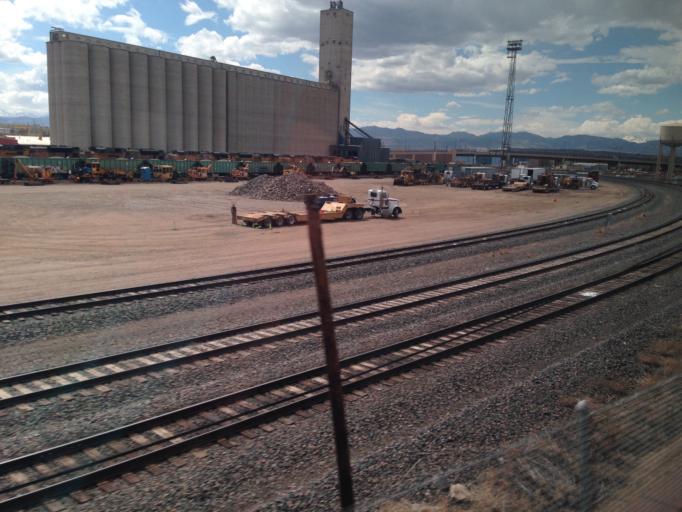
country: US
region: Colorado
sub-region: Adams County
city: Twin Lakes
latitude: 39.8025
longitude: -105.0009
